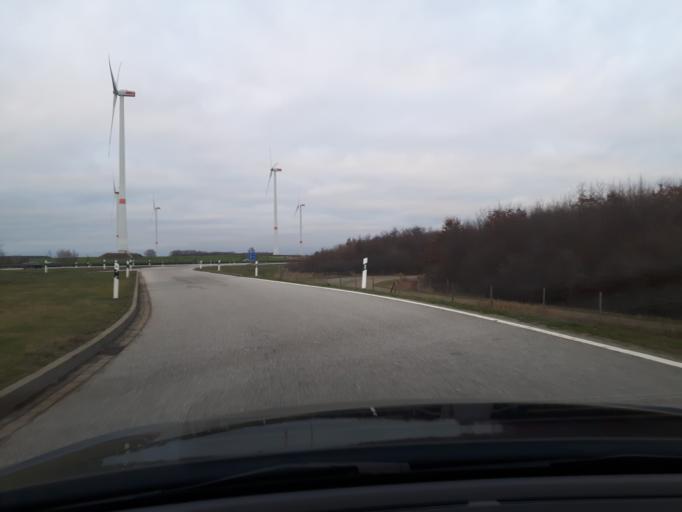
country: DE
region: Mecklenburg-Vorpommern
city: Satow-Oberhagen
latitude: 53.9937
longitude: 11.9455
